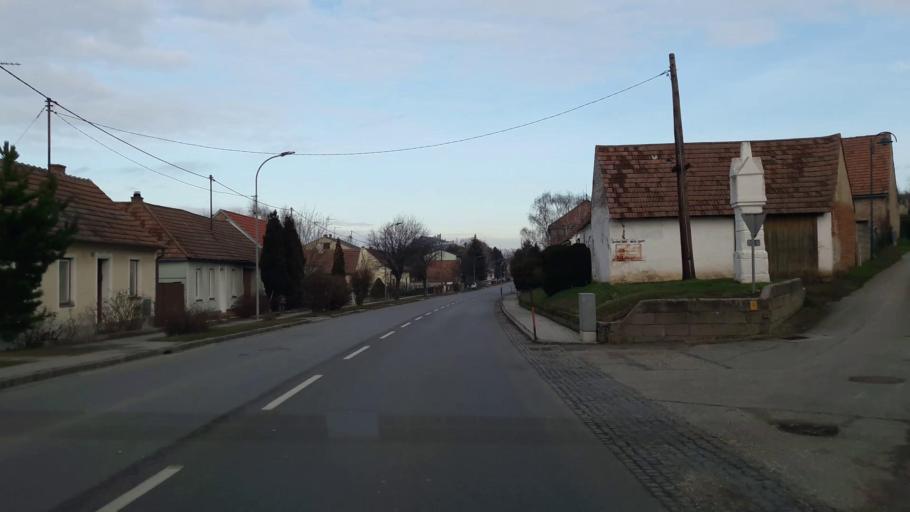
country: AT
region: Lower Austria
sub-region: Politischer Bezirk Mistelbach
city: Staatz
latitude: 48.6586
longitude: 16.4962
